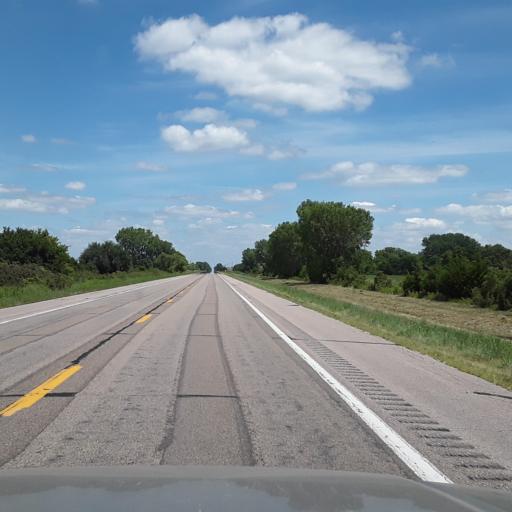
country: US
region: Nebraska
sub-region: Platte County
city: Columbus
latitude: 41.3683
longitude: -97.5404
